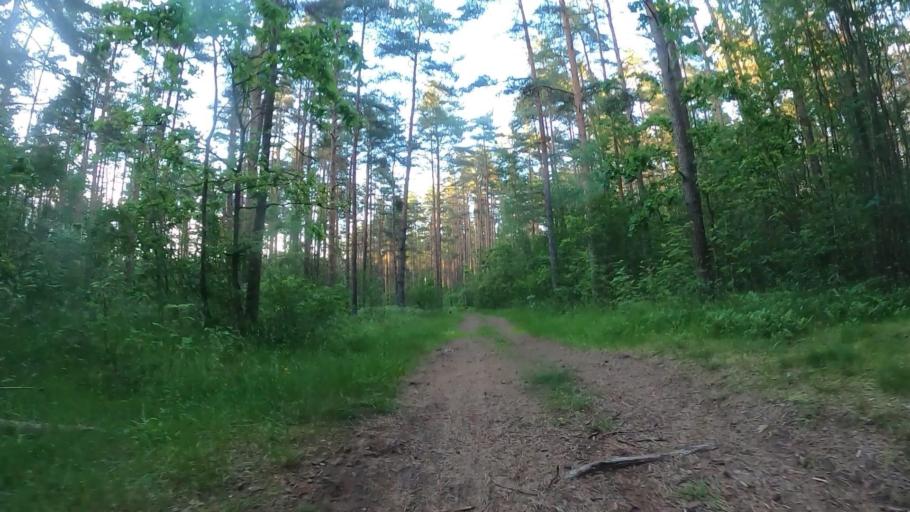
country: LV
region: Marupe
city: Marupe
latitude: 56.8850
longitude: 24.0309
